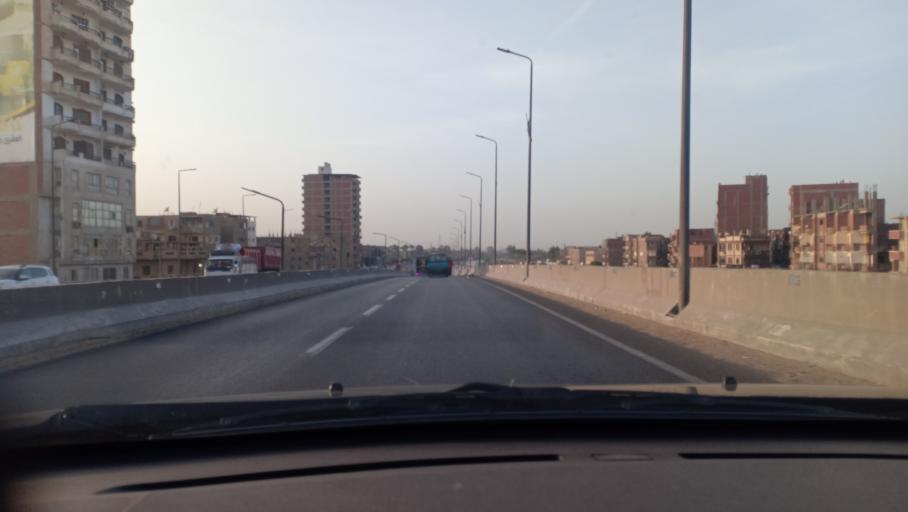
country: EG
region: Muhafazat al Minufiyah
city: Quwaysina
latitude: 30.5491
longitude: 31.2691
